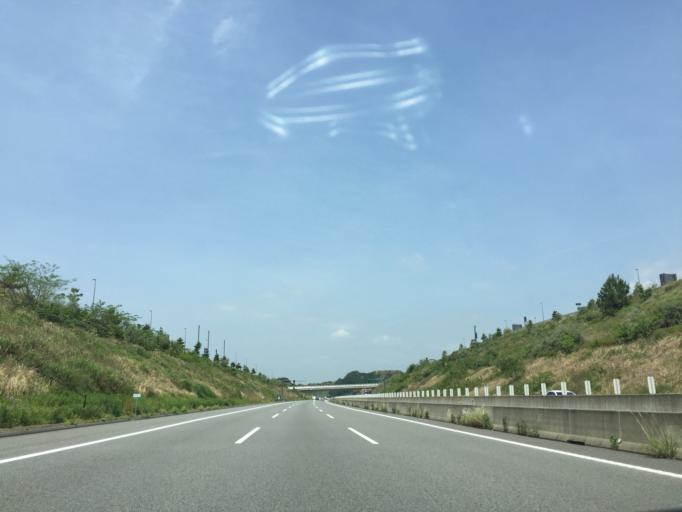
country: JP
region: Shizuoka
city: Mori
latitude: 34.8245
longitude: 137.9079
